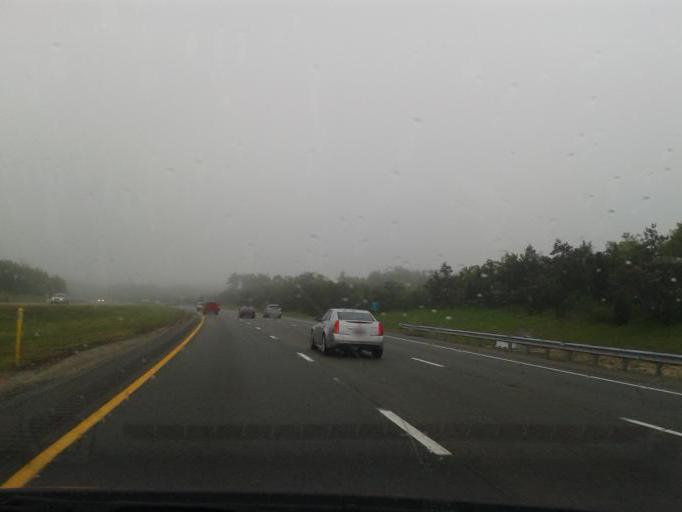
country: US
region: Massachusetts
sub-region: Barnstable County
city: Bourne
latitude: 41.7672
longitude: -70.5880
